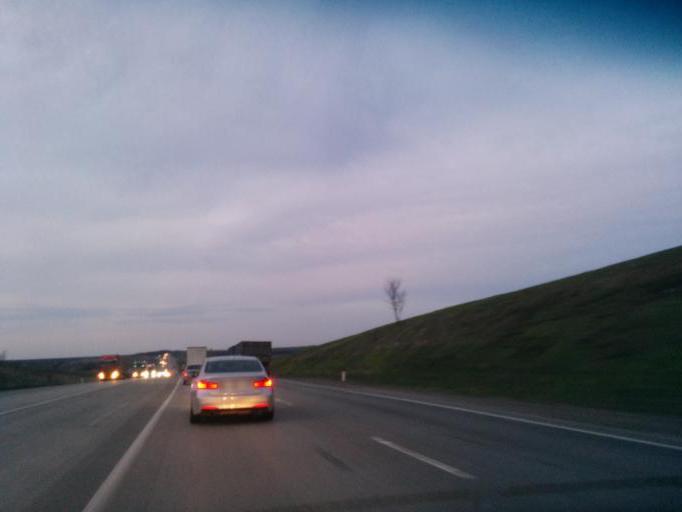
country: RU
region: Rostov
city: Grushevskaya
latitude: 47.5218
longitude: 39.9706
